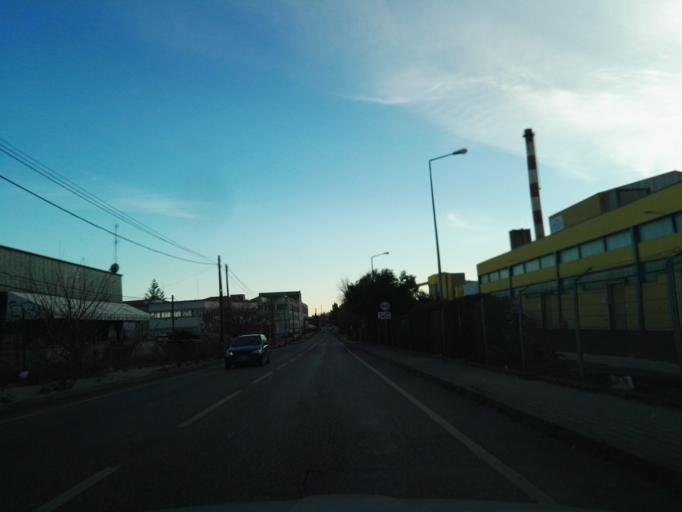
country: PT
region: Lisbon
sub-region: Loures
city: Santa Iria da Azoia
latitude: 38.8353
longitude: -9.0842
